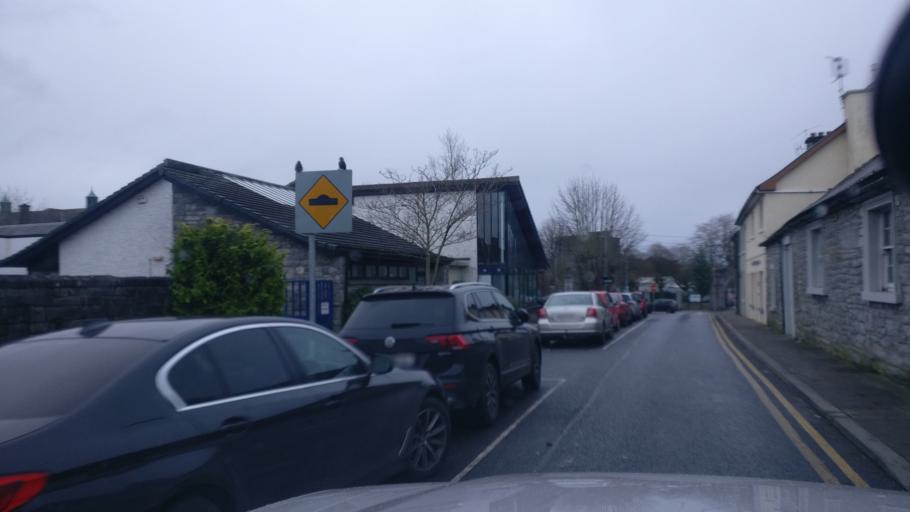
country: IE
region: Connaught
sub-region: County Galway
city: Loughrea
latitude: 53.1981
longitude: -8.5661
